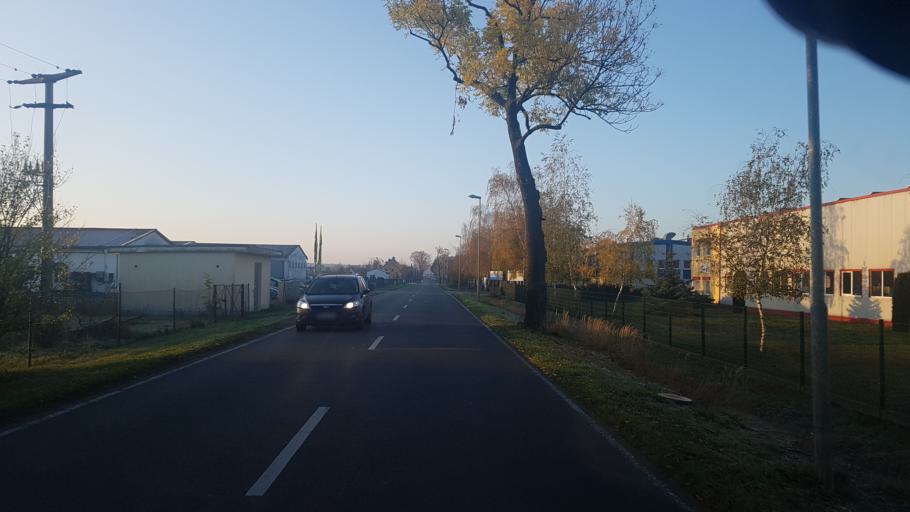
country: DE
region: Saxony
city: Torgau
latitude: 51.4987
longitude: 12.9925
